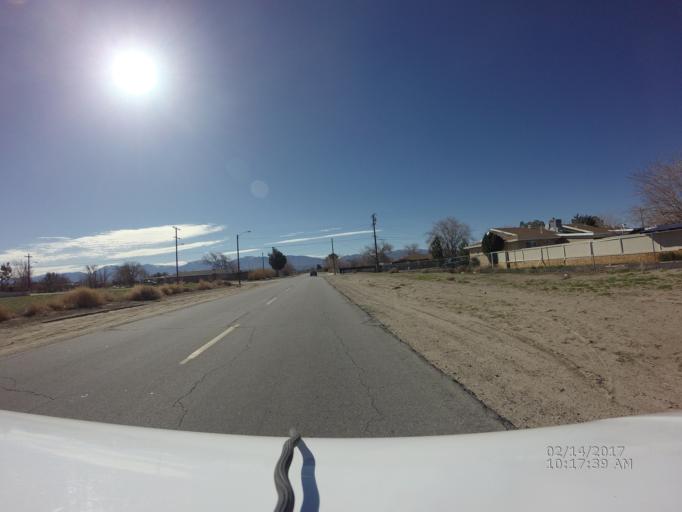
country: US
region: California
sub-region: Los Angeles County
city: Littlerock
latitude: 34.5767
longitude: -117.9520
